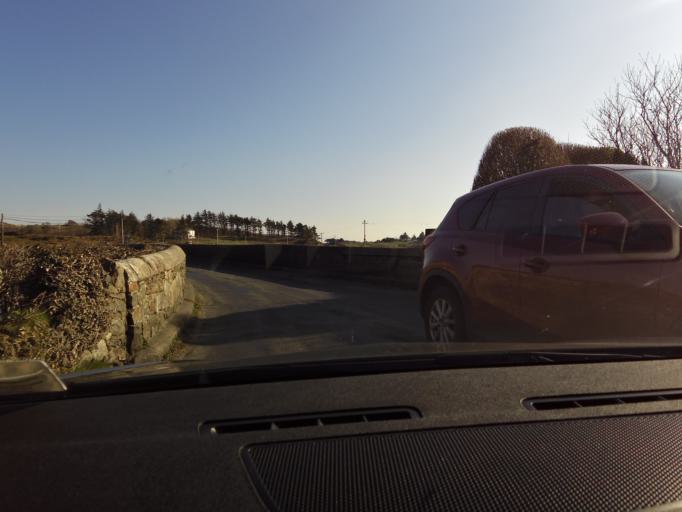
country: IE
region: Connaught
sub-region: County Galway
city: Clifden
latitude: 53.4740
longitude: -10.0196
